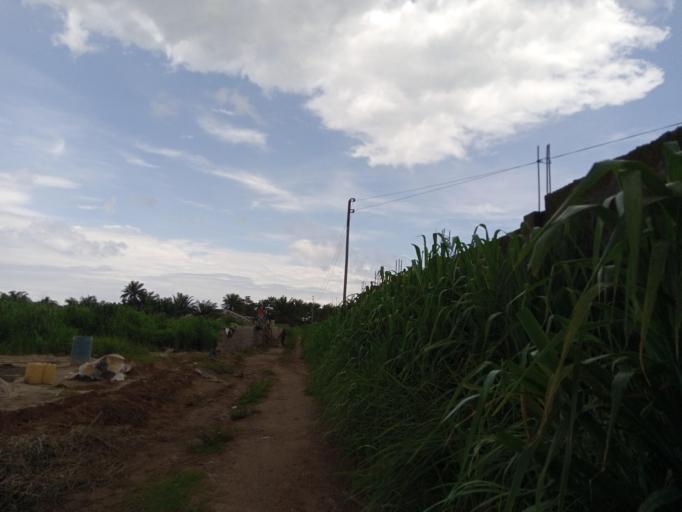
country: SL
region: Northern Province
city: Masoyila
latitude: 8.5821
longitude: -13.1641
